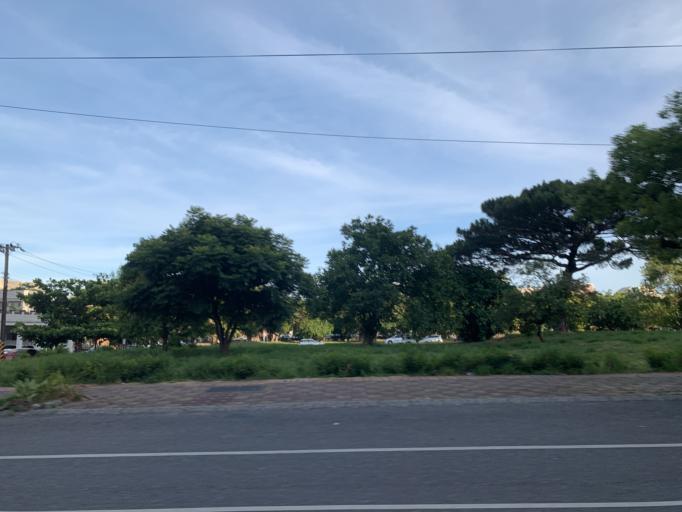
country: TW
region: Taiwan
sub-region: Hualien
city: Hualian
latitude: 23.9904
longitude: 121.6248
